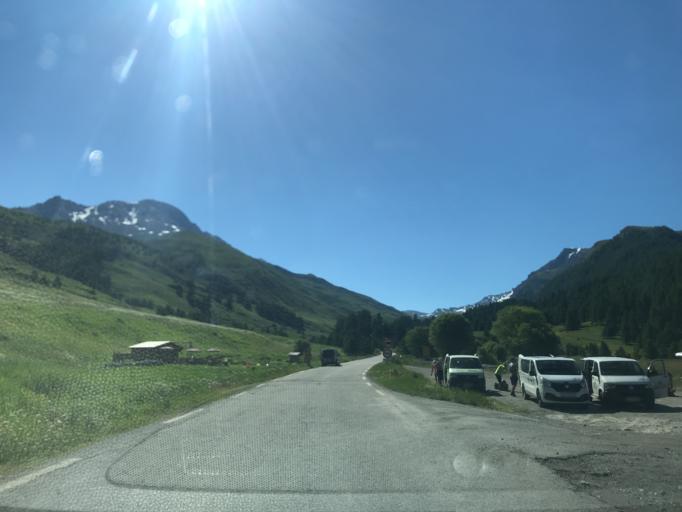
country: IT
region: Piedmont
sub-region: Provincia di Cuneo
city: Pontechianale
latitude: 44.7194
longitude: 6.9035
